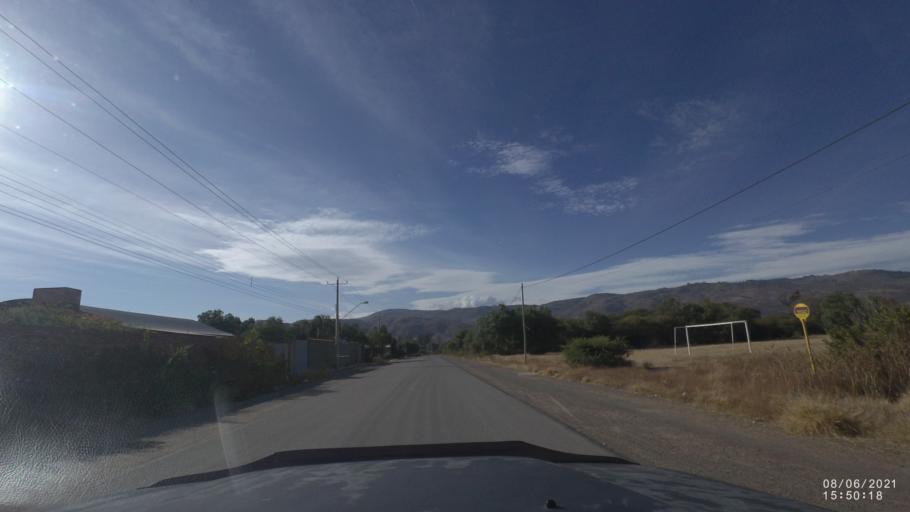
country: BO
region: Cochabamba
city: Capinota
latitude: -17.5582
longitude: -66.2501
